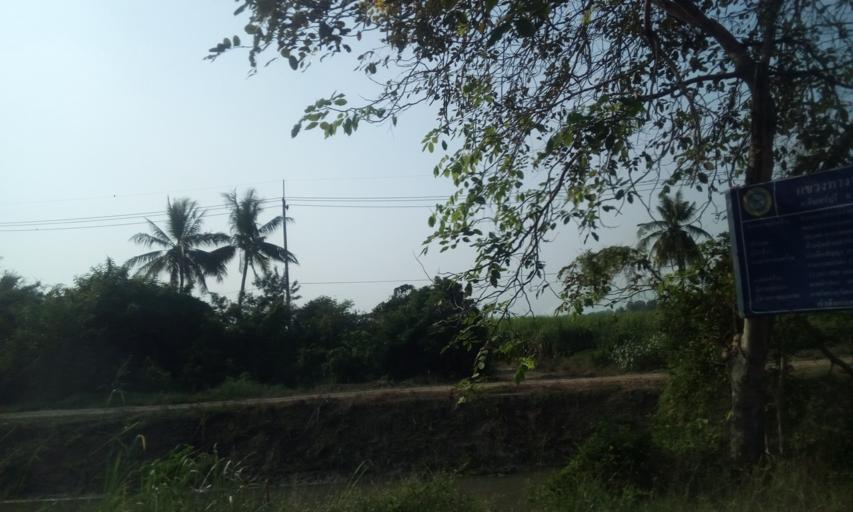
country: TH
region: Sing Buri
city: Phrom Buri
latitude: 14.7469
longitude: 100.4408
